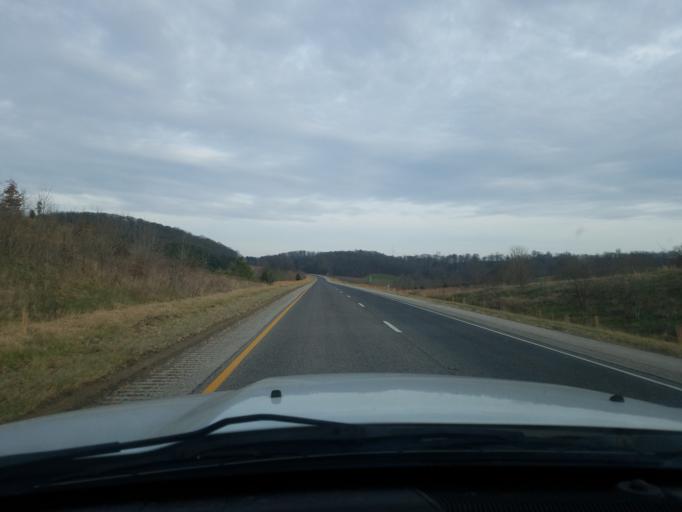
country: US
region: Indiana
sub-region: Dubois County
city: Ferdinand
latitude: 38.2118
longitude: -86.7604
